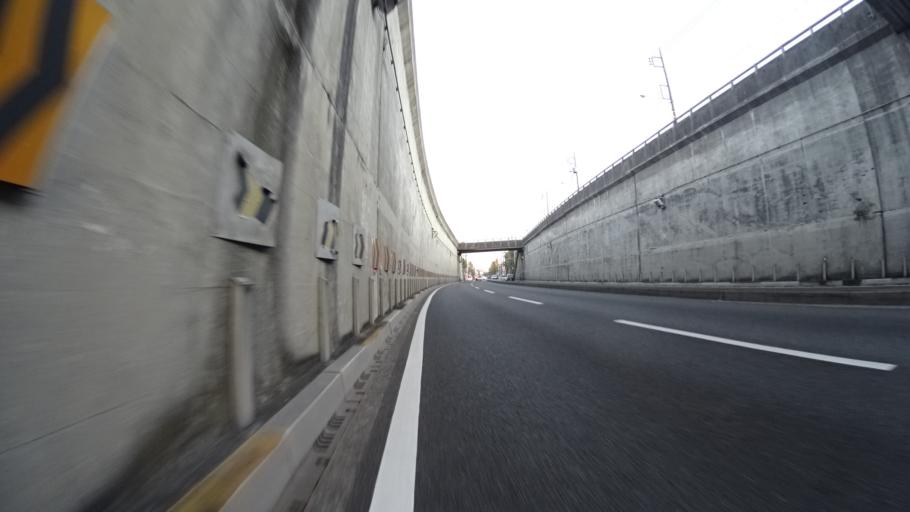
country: JP
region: Tokyo
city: Hino
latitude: 35.7004
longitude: 139.3644
